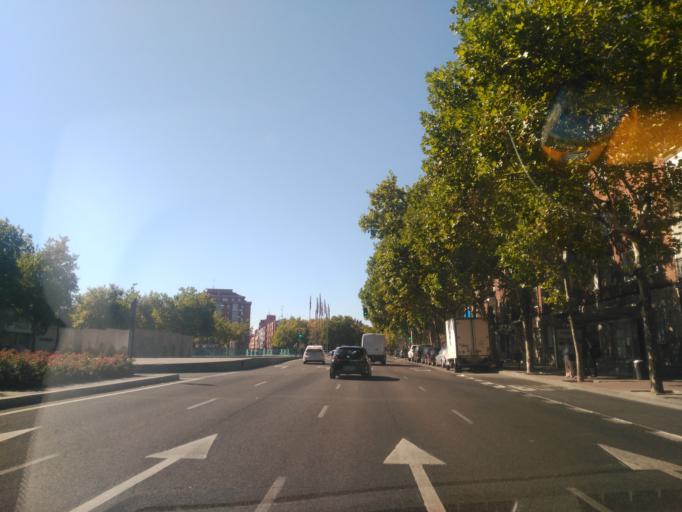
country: ES
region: Castille and Leon
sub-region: Provincia de Valladolid
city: Valladolid
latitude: 41.6320
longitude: -4.7405
